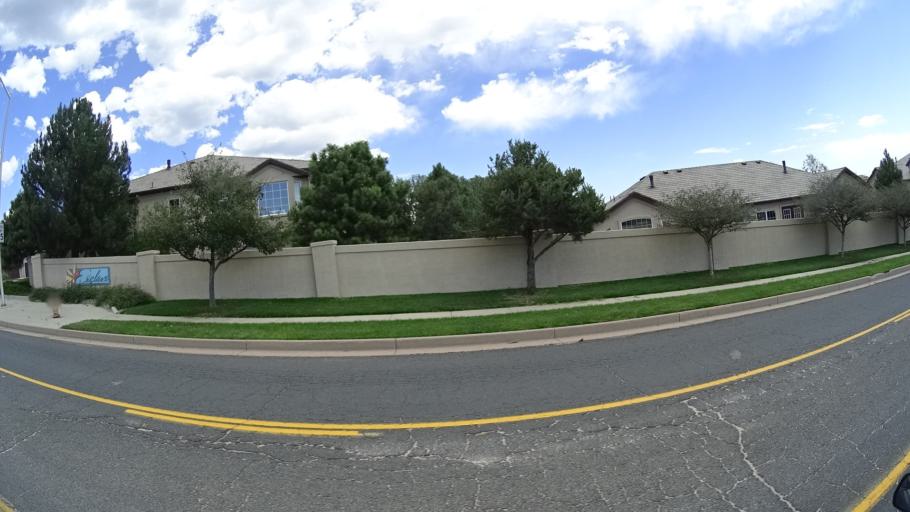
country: US
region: Colorado
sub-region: El Paso County
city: Fort Carson
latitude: 38.7622
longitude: -104.8198
